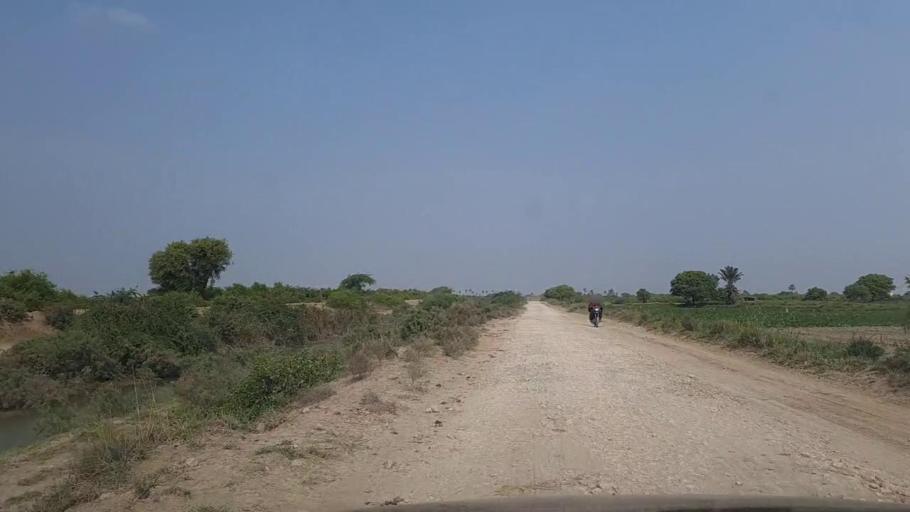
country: PK
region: Sindh
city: Thatta
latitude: 24.7484
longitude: 67.8076
